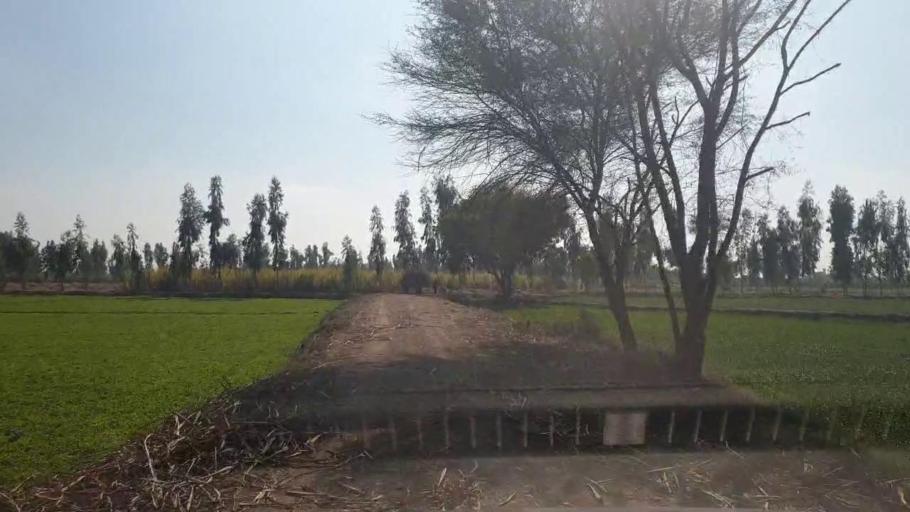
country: PK
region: Sindh
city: Shahdadpur
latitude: 25.9252
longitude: 68.5752
